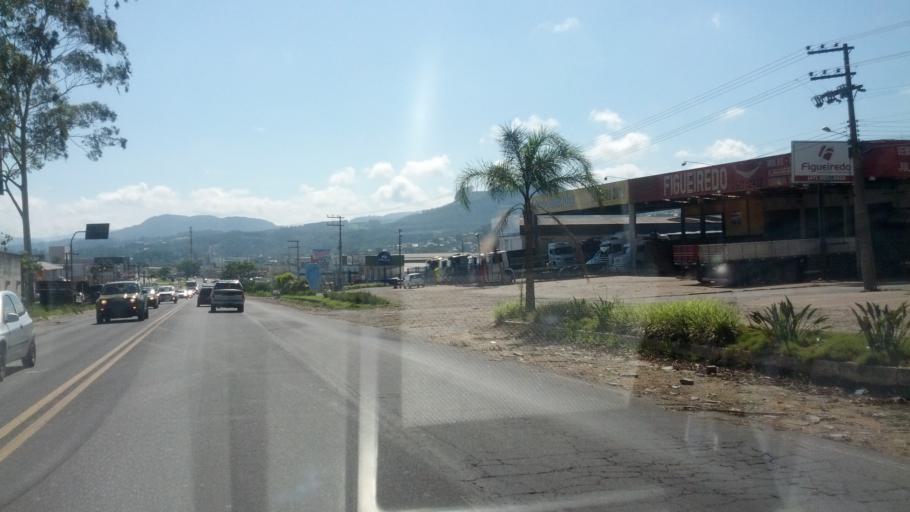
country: BR
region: Santa Catarina
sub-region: Rio Do Sul
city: Rio do Sul
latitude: -27.2052
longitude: -49.6431
